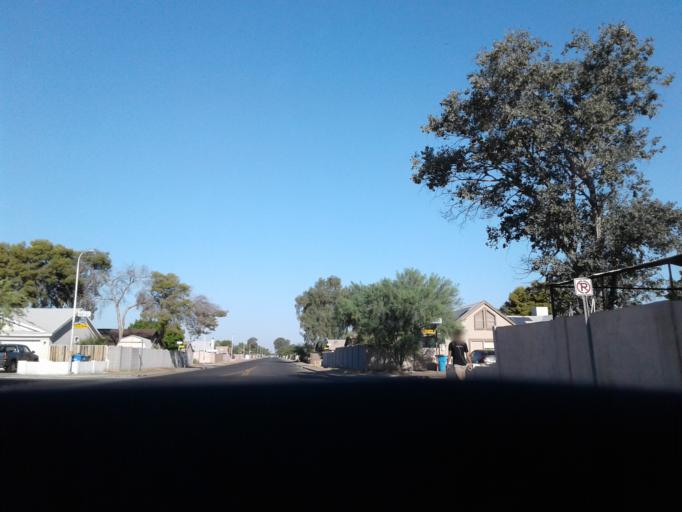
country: US
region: Arizona
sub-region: Maricopa County
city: Tolleson
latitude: 33.4589
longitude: -112.1868
